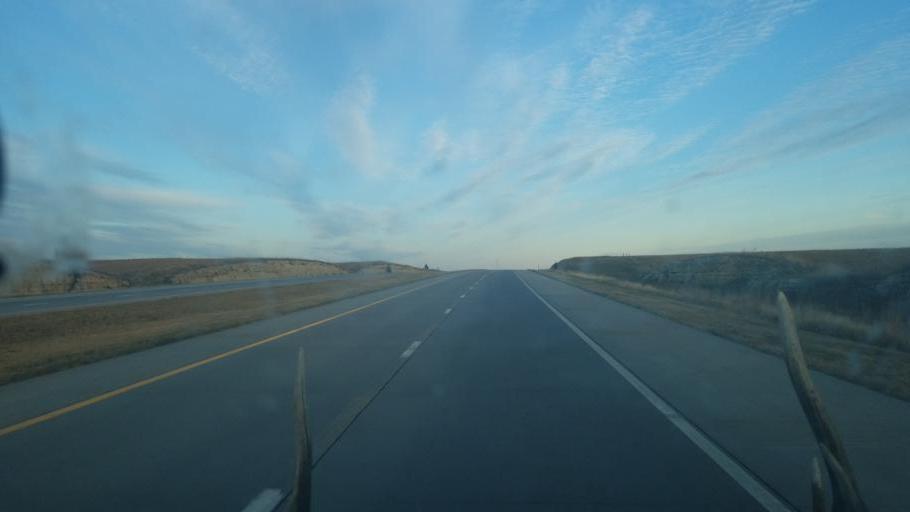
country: US
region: Kansas
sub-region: Riley County
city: Manhattan
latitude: 39.0660
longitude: -96.5872
